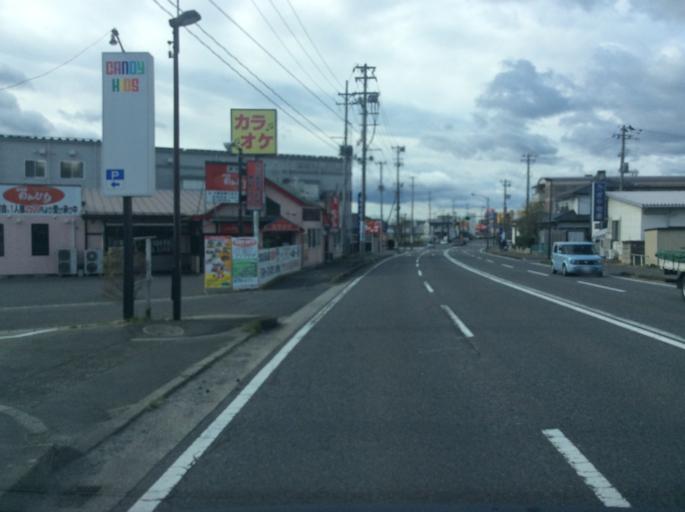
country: JP
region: Fukushima
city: Koriyama
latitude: 37.3871
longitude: 140.3934
